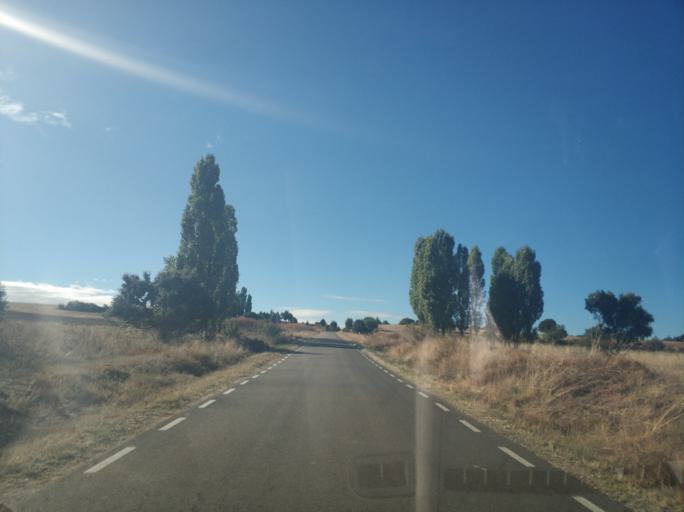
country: ES
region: Castille and Leon
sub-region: Provincia de Burgos
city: San Juan del Monte
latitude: 41.6781
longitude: -3.5243
